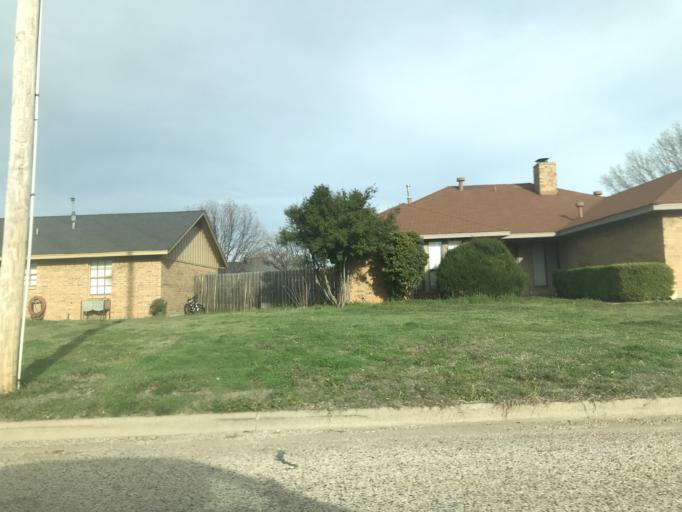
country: US
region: Texas
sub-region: Taylor County
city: Abilene
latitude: 32.3966
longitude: -99.7705
